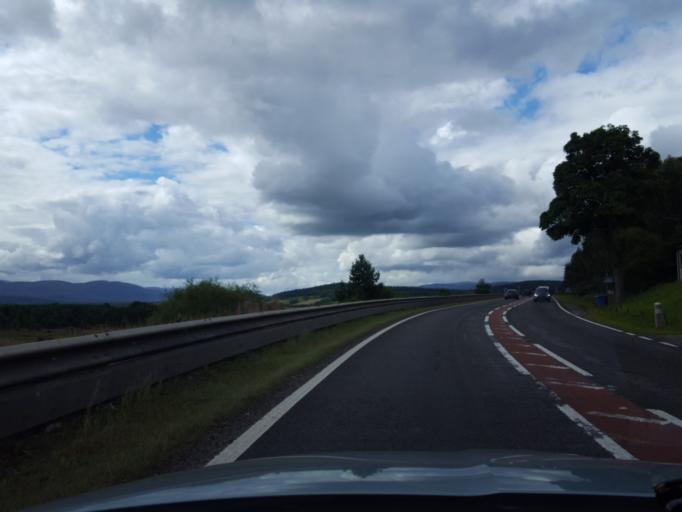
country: GB
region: Scotland
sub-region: Highland
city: Grantown on Spey
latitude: 57.3098
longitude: -3.6355
